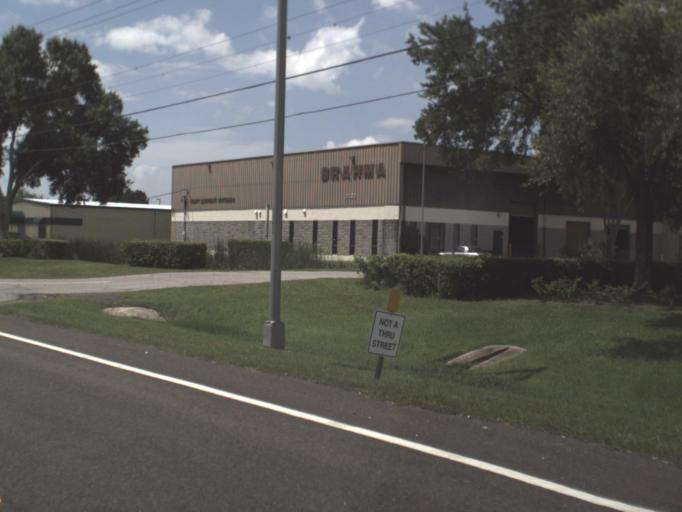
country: US
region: Florida
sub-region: Hillsborough County
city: East Lake-Orient Park
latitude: 27.9647
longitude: -82.3605
